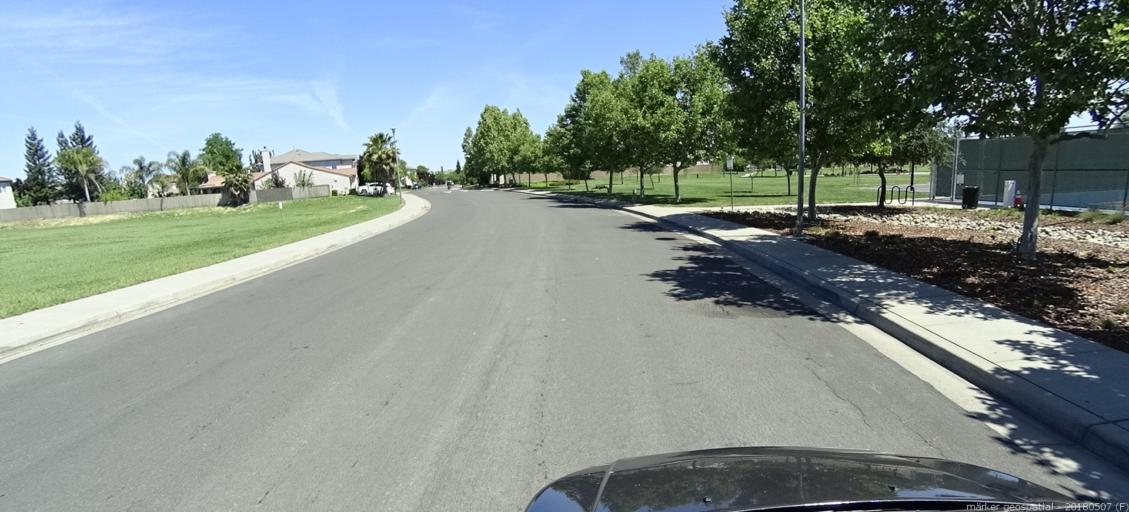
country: US
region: California
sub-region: Sacramento County
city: Elverta
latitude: 38.6720
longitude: -121.5106
